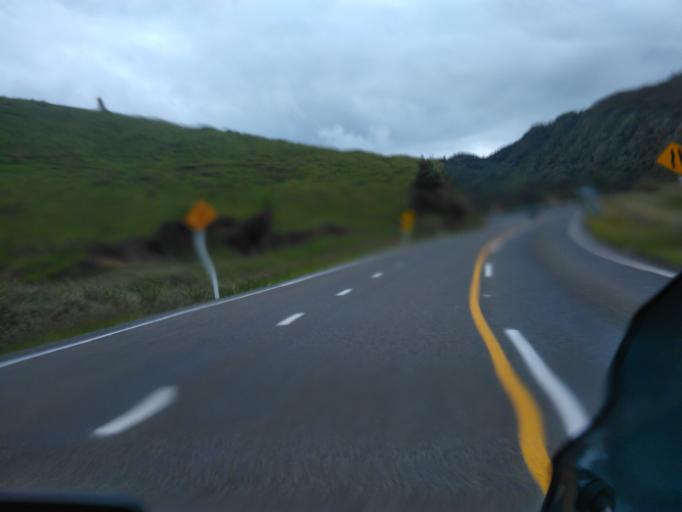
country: NZ
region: Bay of Plenty
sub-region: Opotiki District
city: Opotiki
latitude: -38.3529
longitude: 177.4507
